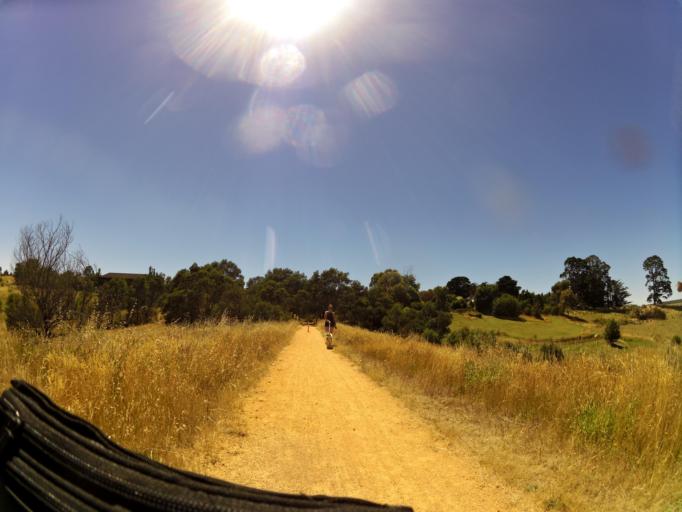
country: AU
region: Victoria
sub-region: Ballarat North
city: Delacombe
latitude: -37.7031
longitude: 143.6399
